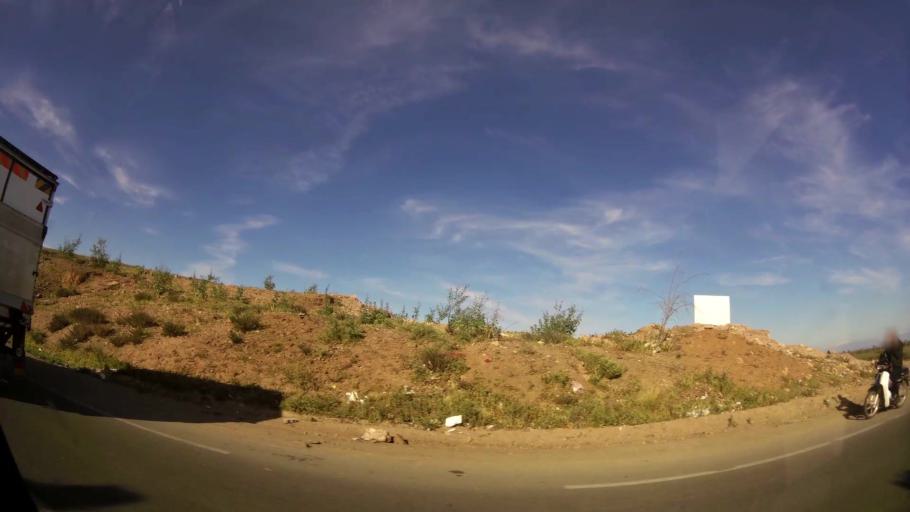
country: MA
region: Marrakech-Tensift-Al Haouz
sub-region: Marrakech
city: Marrakesh
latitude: 31.7021
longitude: -8.0616
